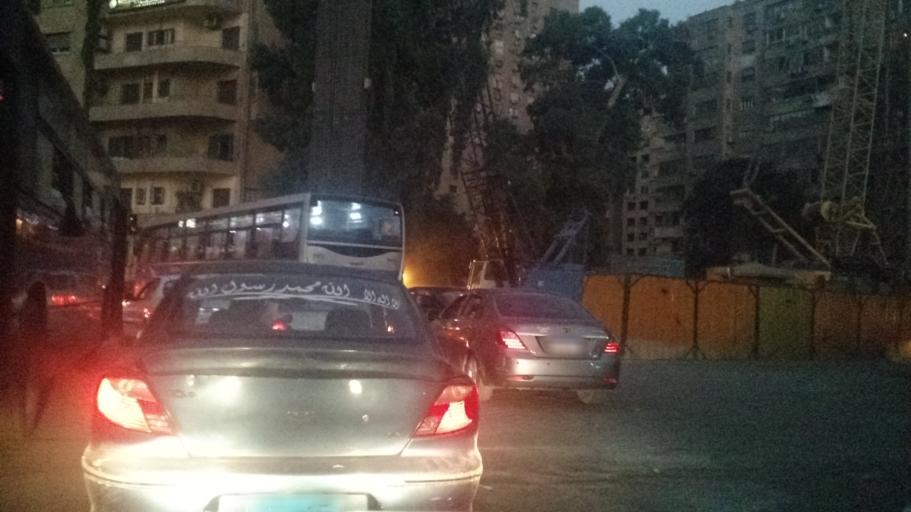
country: EG
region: Al Jizah
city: Al Jizah
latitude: 30.0281
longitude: 31.2161
